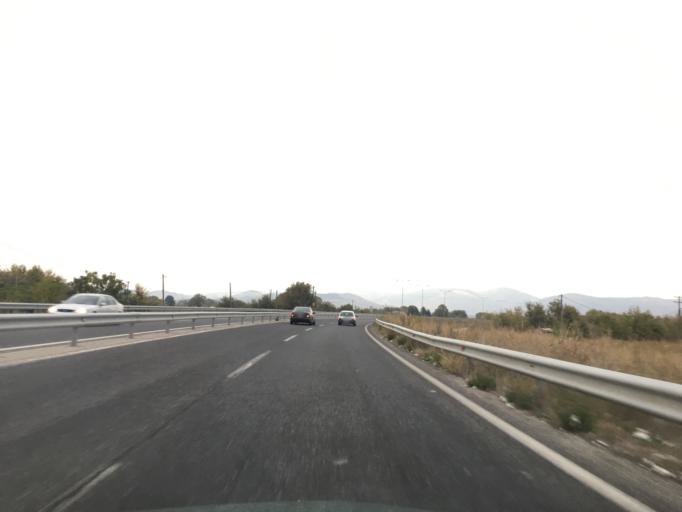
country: GR
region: Thessaly
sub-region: Trikala
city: Trikala
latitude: 39.5615
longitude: 21.8022
